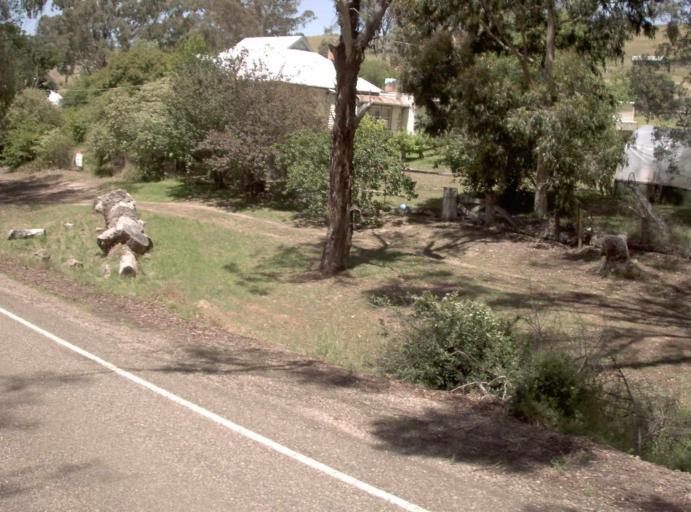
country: AU
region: Victoria
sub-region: East Gippsland
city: Bairnsdale
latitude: -37.3683
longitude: 147.8346
